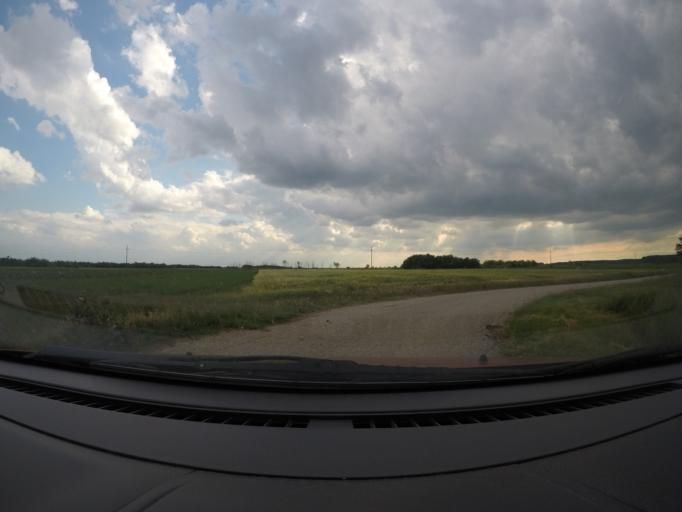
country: RS
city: Uzdin
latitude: 45.2027
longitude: 20.6085
